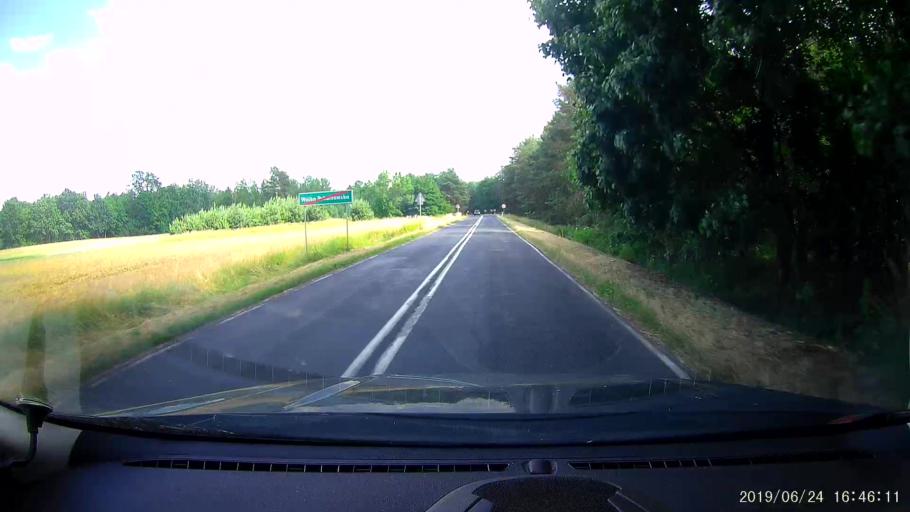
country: PL
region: Lublin Voivodeship
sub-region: Powiat tomaszowski
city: Laszczow
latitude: 50.5278
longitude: 23.6746
